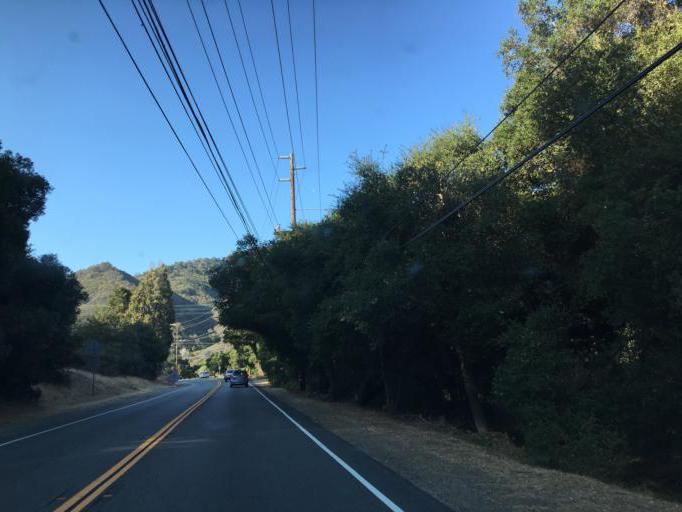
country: US
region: California
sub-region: Los Angeles County
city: Malibu Beach
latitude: 34.0851
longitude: -118.7045
